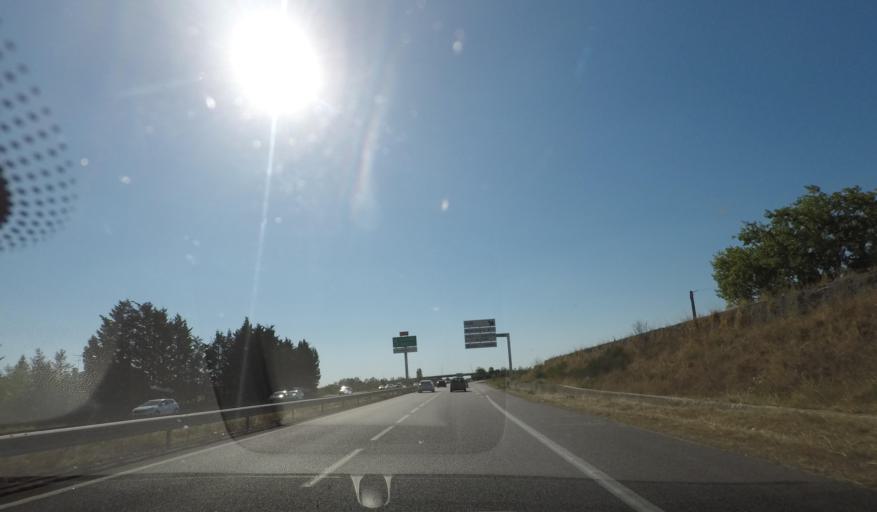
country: FR
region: Pays de la Loire
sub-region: Departement de la Loire-Atlantique
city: Montoir-de-Bretagne
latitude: 47.3242
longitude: -2.1583
